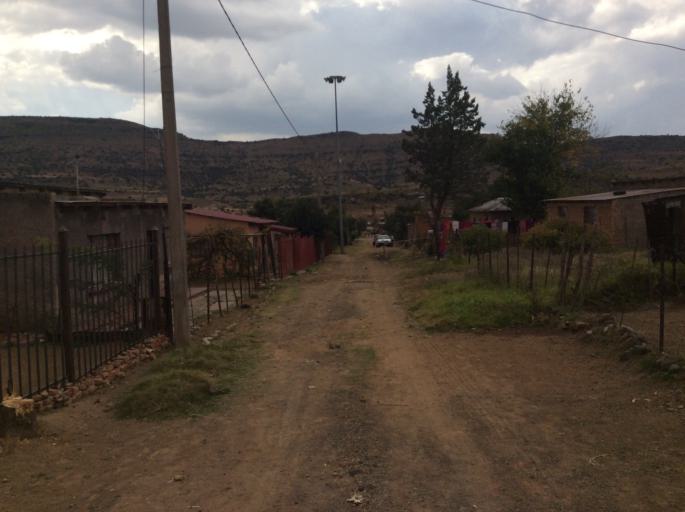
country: LS
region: Mafeteng
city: Mafeteng
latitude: -29.7213
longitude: 27.0317
